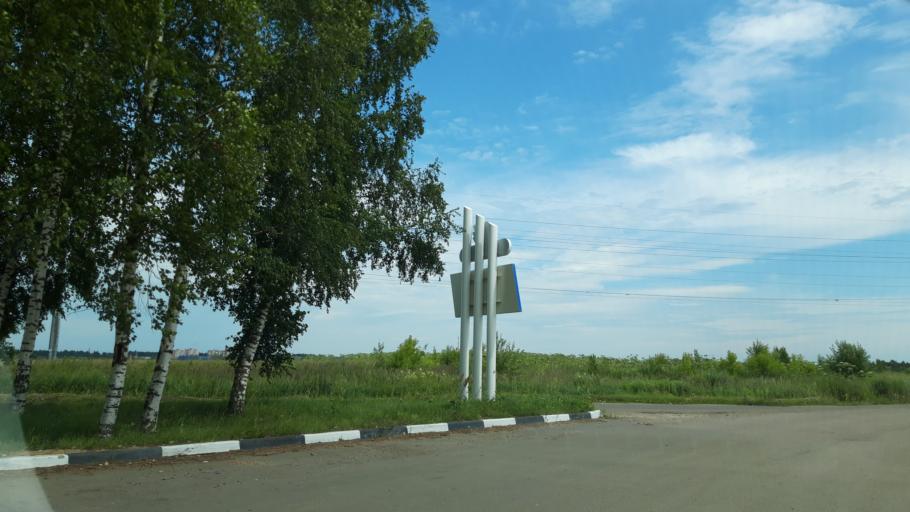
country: RU
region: Moskovskaya
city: Radumlya
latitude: 56.0574
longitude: 37.1216
